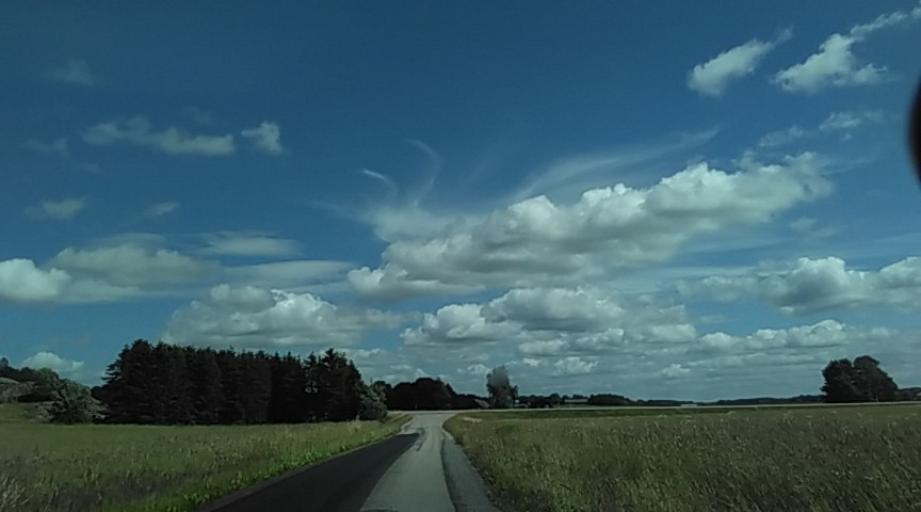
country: SE
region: Vaestra Goetaland
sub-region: Vargarda Kommun
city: Vargarda
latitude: 58.1382
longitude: 12.8587
